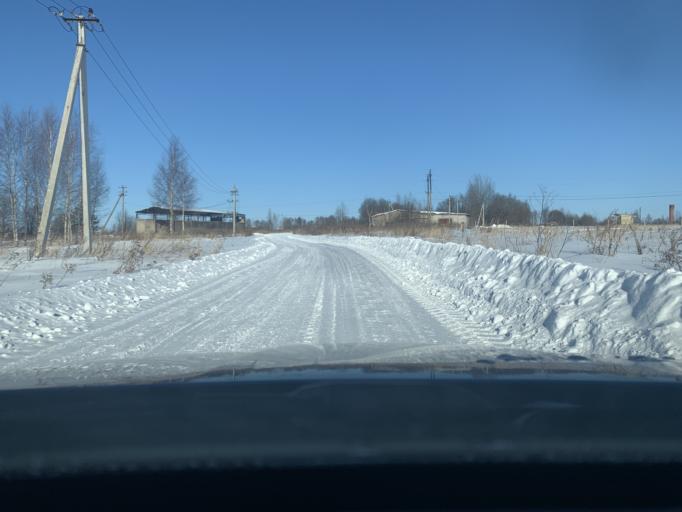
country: RU
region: Jaroslavl
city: Tunoshna
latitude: 57.6530
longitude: 40.0678
